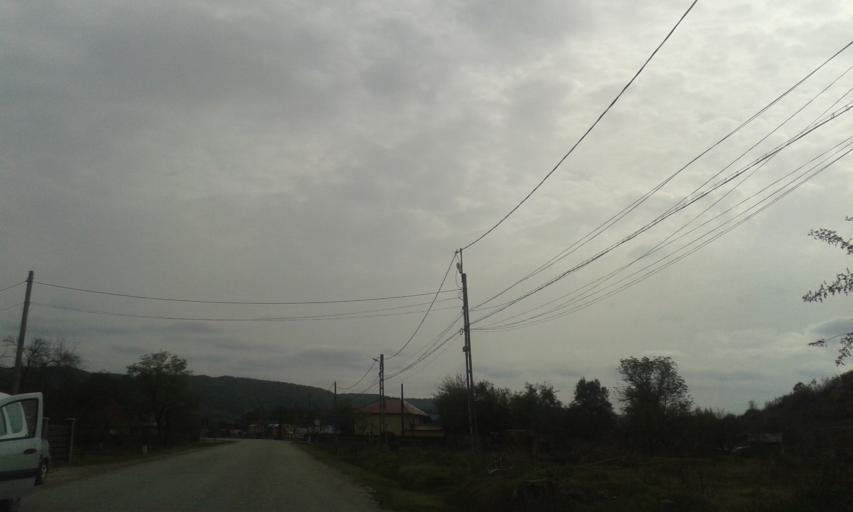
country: RO
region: Gorj
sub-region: Comuna Hurezani
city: Hurezani
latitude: 44.8184
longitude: 23.6519
